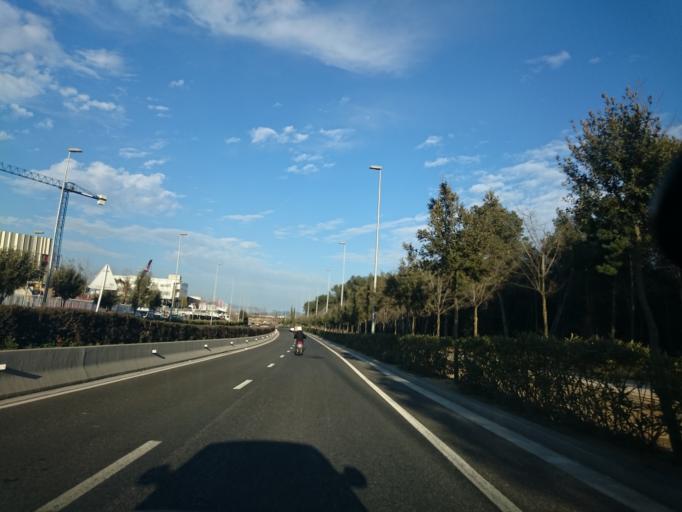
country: ES
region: Catalonia
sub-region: Provincia de Barcelona
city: Sant Cugat del Valles
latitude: 41.4829
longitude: 2.1074
